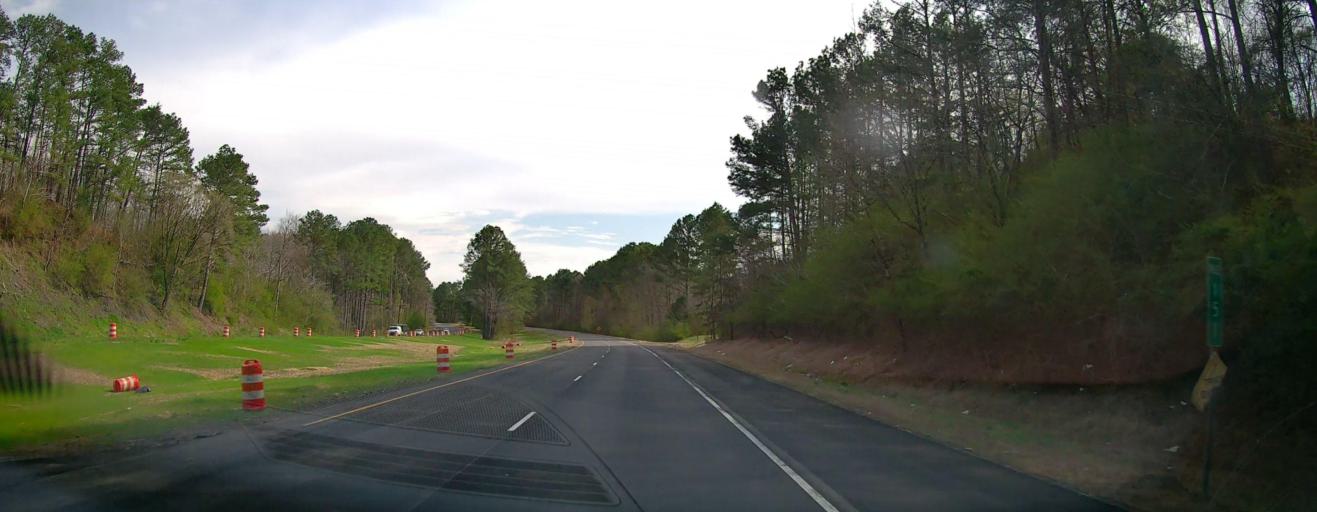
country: US
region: Alabama
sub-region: Walker County
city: Sumiton
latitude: 33.7026
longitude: -86.9918
